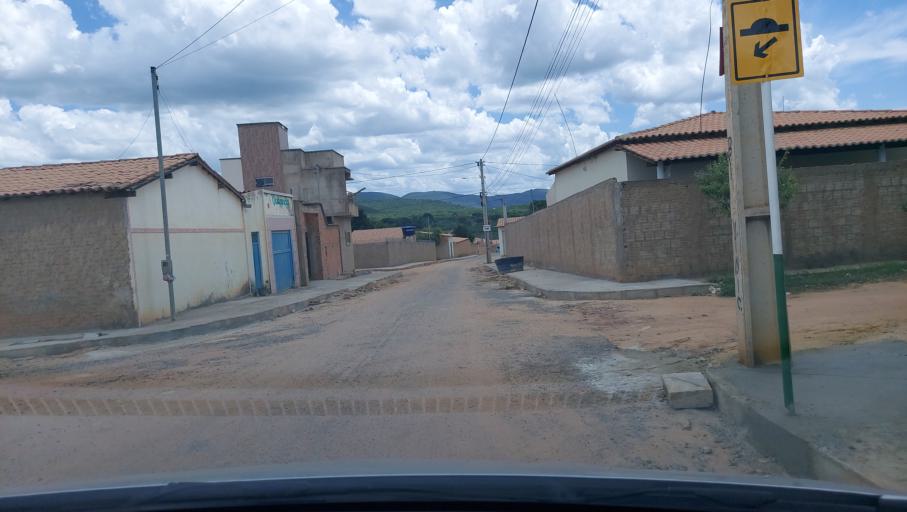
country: BR
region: Bahia
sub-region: Oliveira Dos Brejinhos
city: Beira Rio
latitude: -12.0057
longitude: -42.6310
